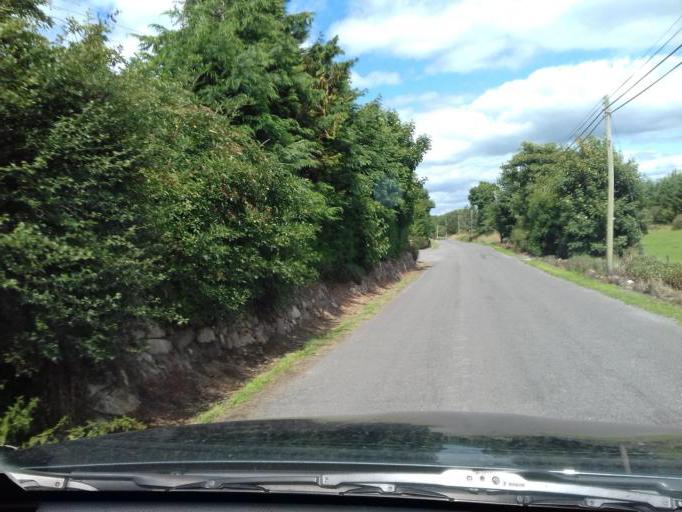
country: IE
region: Munster
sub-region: Waterford
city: Tra Mhor
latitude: 52.1728
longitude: -7.2369
